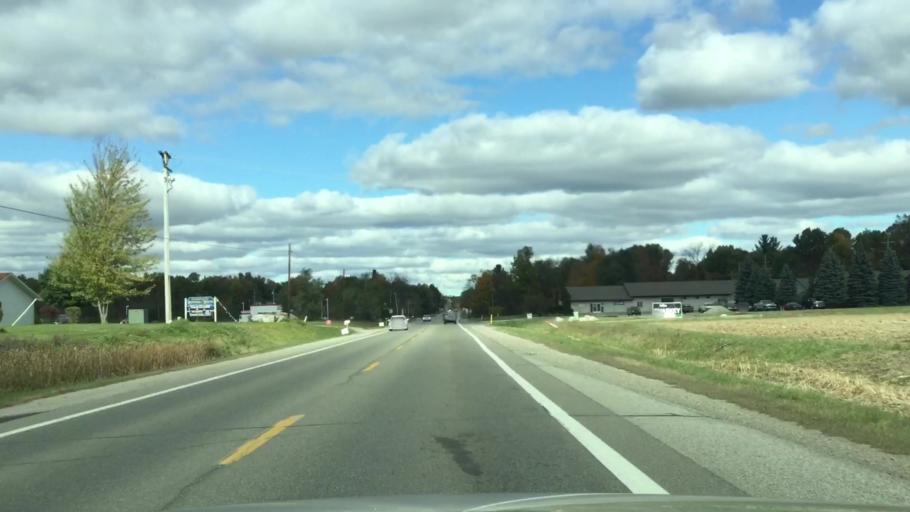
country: US
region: Michigan
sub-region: Lapeer County
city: Barnes Lake-Millers Lake
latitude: 43.1948
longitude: -83.3127
